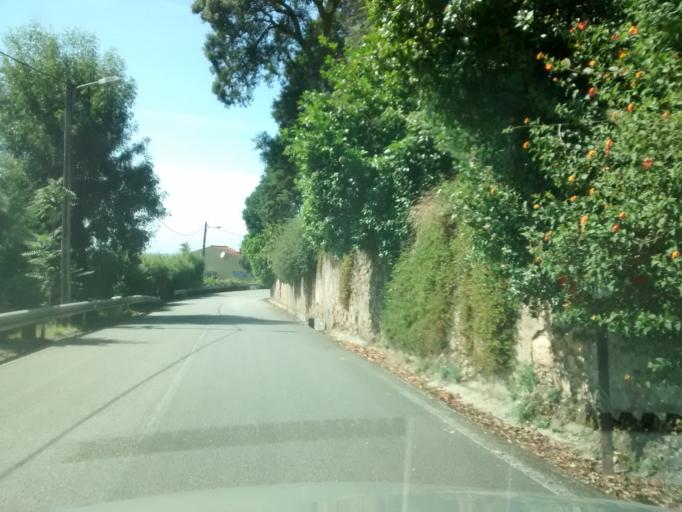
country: PT
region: Aveiro
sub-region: Mealhada
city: Pampilhosa do Botao
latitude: 40.3801
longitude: -8.3763
